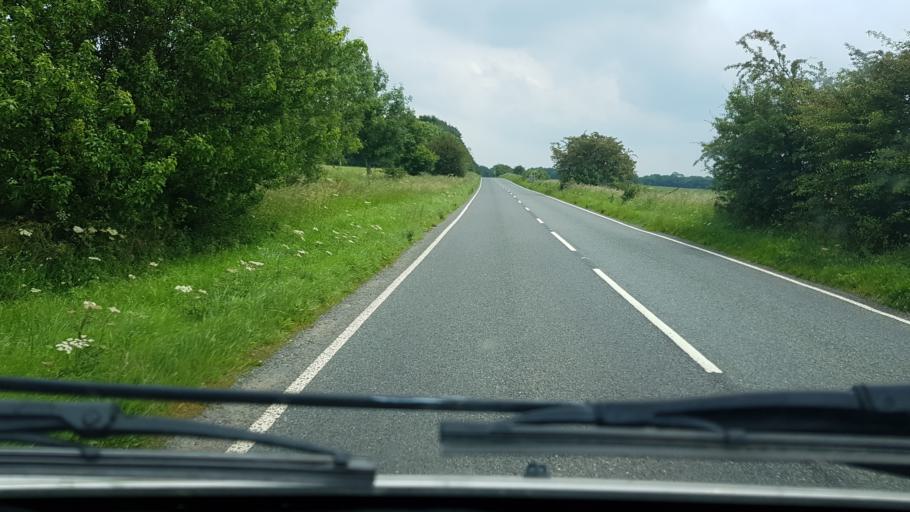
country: GB
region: England
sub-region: Gloucestershire
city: Chipping Campden
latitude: 51.9900
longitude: -1.7752
